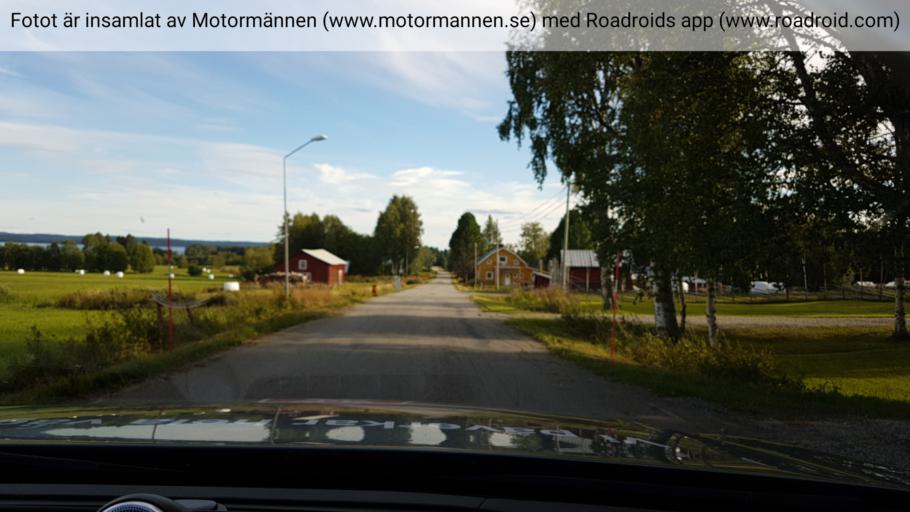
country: SE
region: Jaemtland
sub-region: Stroemsunds Kommun
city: Stroemsund
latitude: 64.0808
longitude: 15.8247
